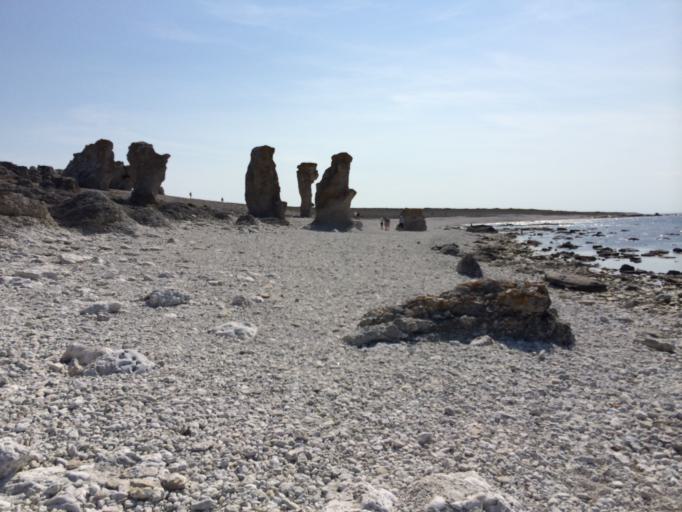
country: SE
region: Gotland
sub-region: Gotland
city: Slite
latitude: 57.9980
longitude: 19.1810
